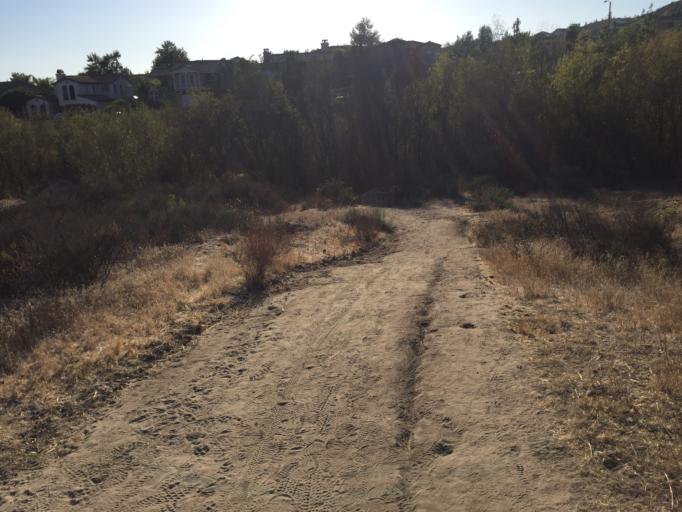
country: US
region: California
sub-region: Ventura County
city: Simi Valley
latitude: 34.2913
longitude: -118.7609
